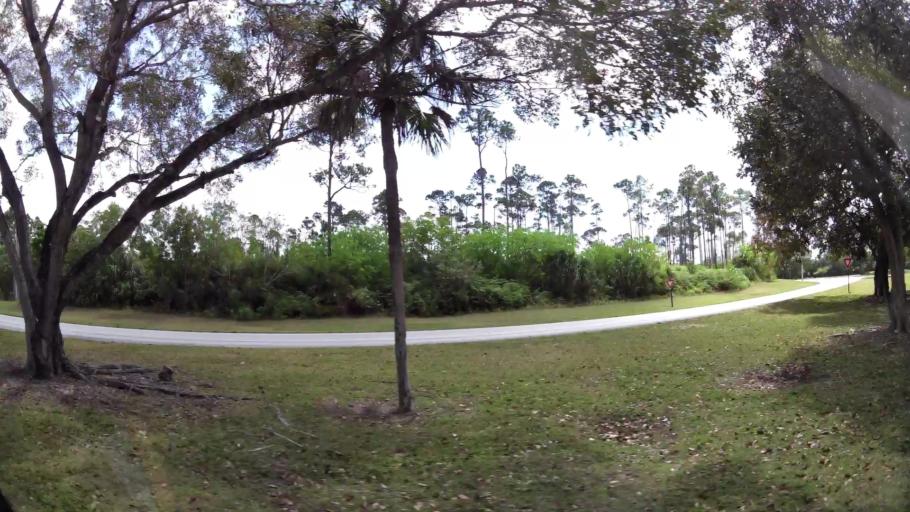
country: BS
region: Freeport
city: Lucaya
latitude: 26.5247
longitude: -78.6592
